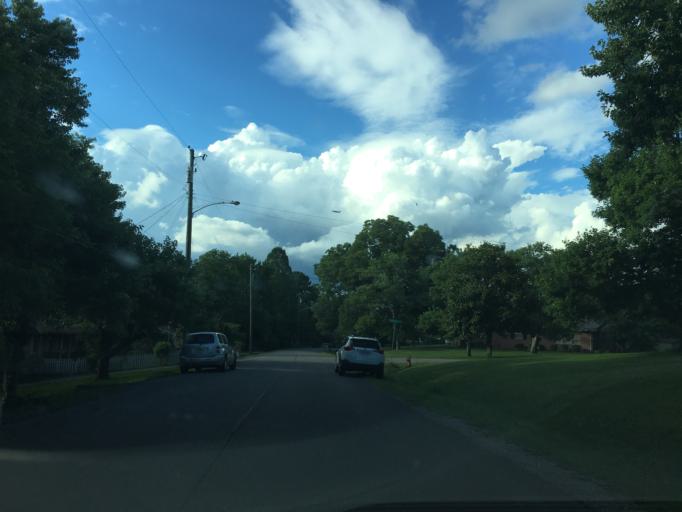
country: US
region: Tennessee
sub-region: Davidson County
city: Oak Hill
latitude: 36.0638
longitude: -86.7214
